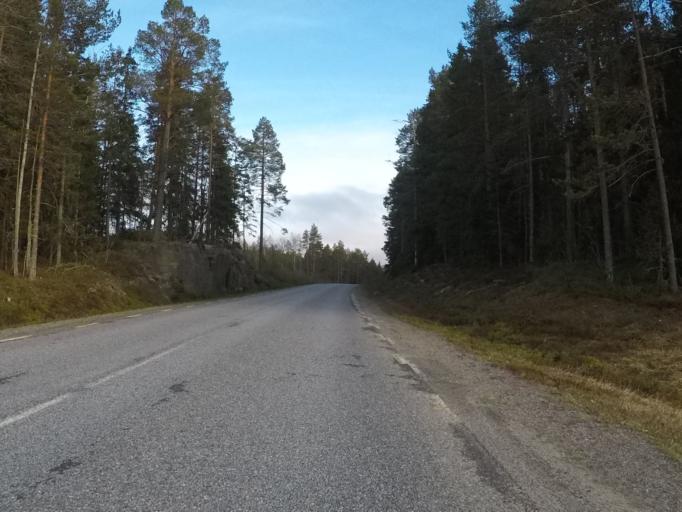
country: SE
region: Vaesterbotten
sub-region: Robertsfors Kommun
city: Robertsfors
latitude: 63.9860
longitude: 20.8121
